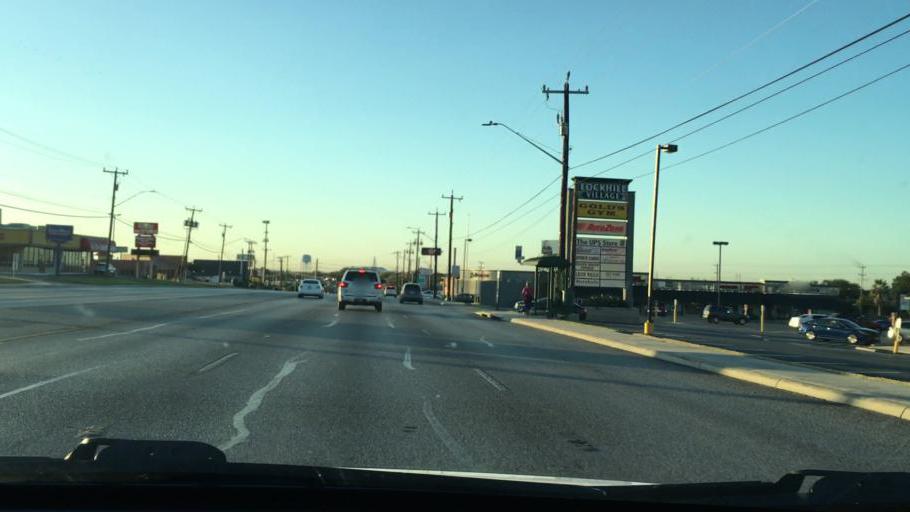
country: US
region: Texas
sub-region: Bexar County
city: Castle Hills
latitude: 29.5442
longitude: -98.5292
